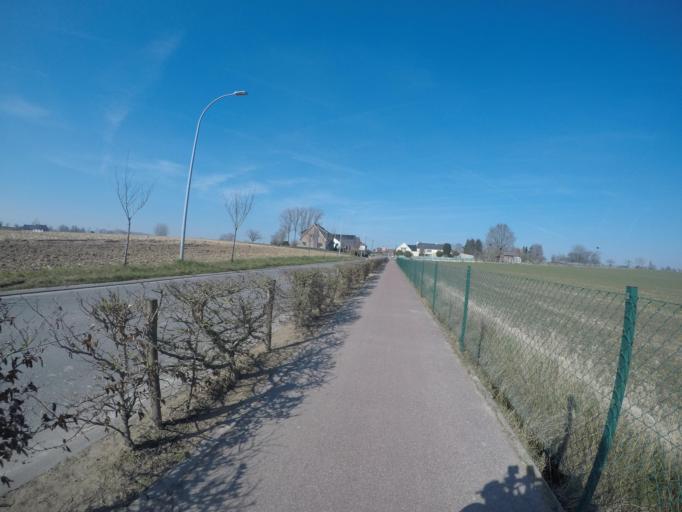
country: BE
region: Flanders
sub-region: Provincie Oost-Vlaanderen
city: Sint-Maria-Lierde
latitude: 50.7977
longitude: 3.8290
